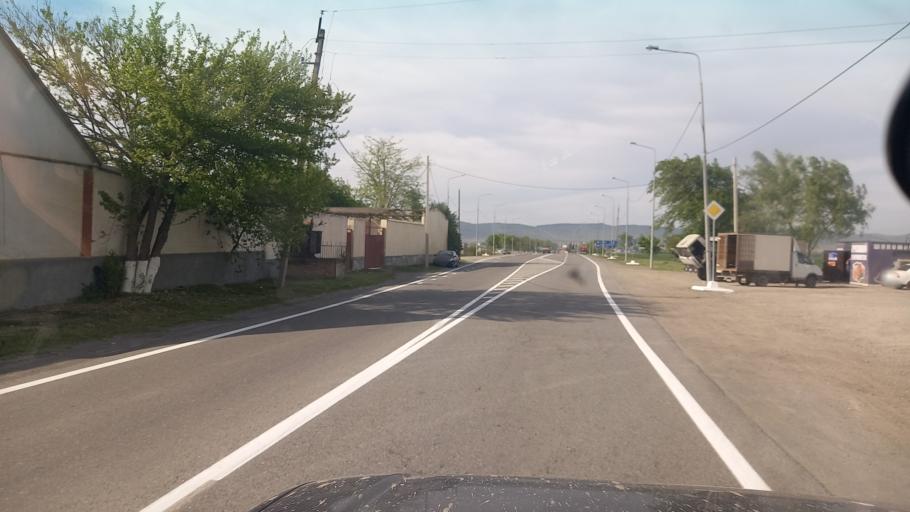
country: RU
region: Ingushetiya
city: Ordzhonikidzevskaya
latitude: 43.2842
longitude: 45.0516
